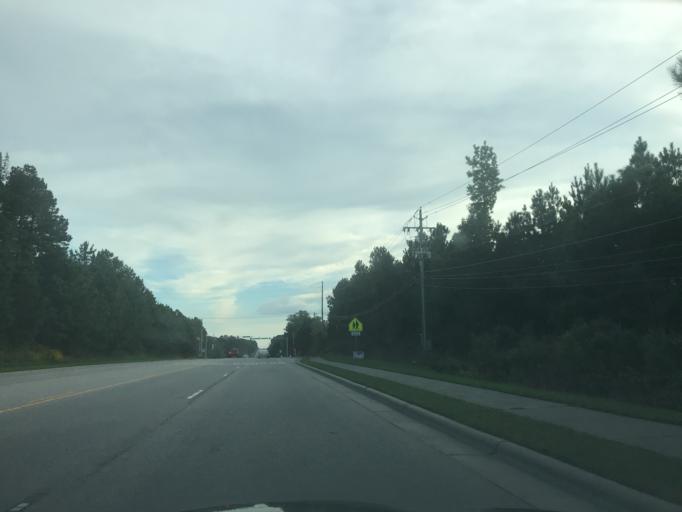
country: US
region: North Carolina
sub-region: Wake County
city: Green Level
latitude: 35.7752
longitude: -78.8731
